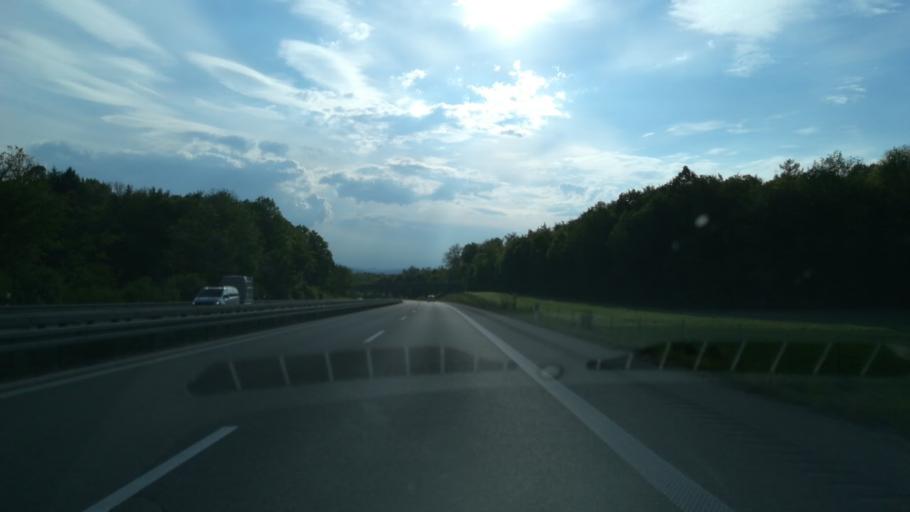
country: DE
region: Baden-Wuerttemberg
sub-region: Freiburg Region
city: Steisslingen
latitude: 47.8254
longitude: 8.9071
